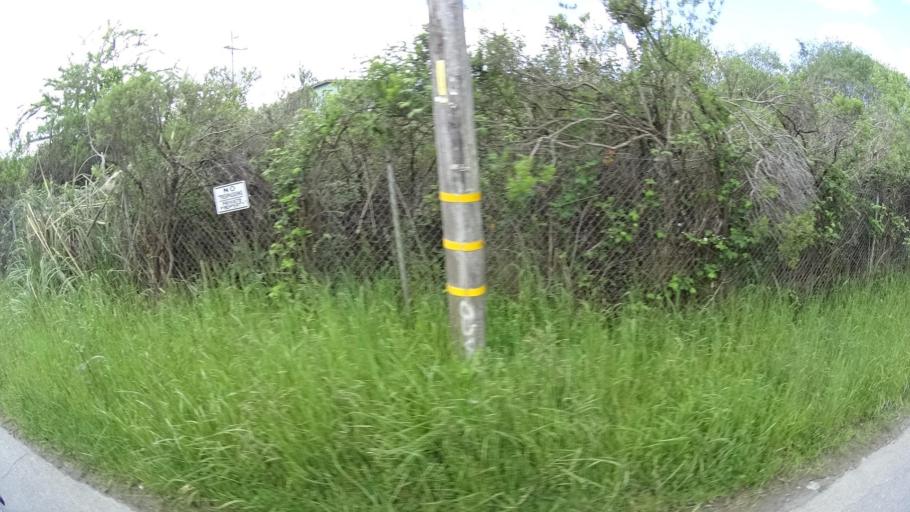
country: US
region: California
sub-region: Humboldt County
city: Blue Lake
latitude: 40.8976
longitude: -124.0079
